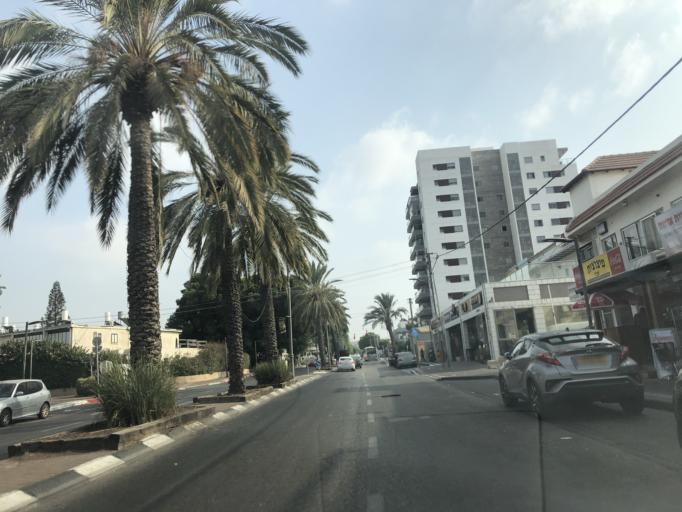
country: IL
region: Central District
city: Rosh Ha'Ayin
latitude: 32.0965
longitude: 34.9436
